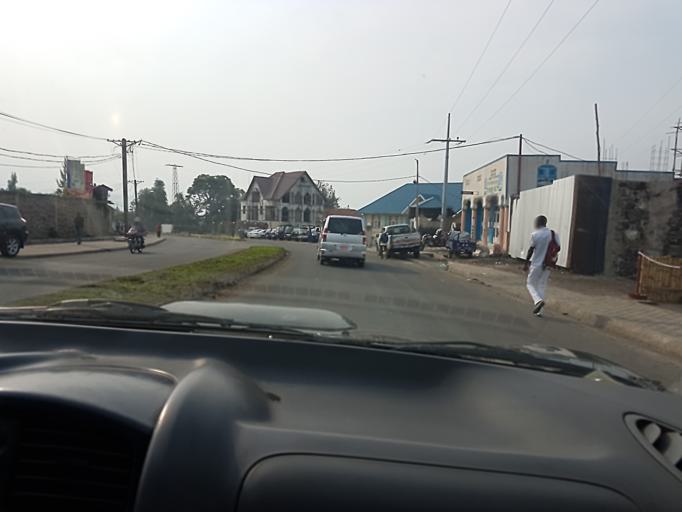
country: CD
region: Nord Kivu
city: Goma
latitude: -1.6865
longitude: 29.2285
